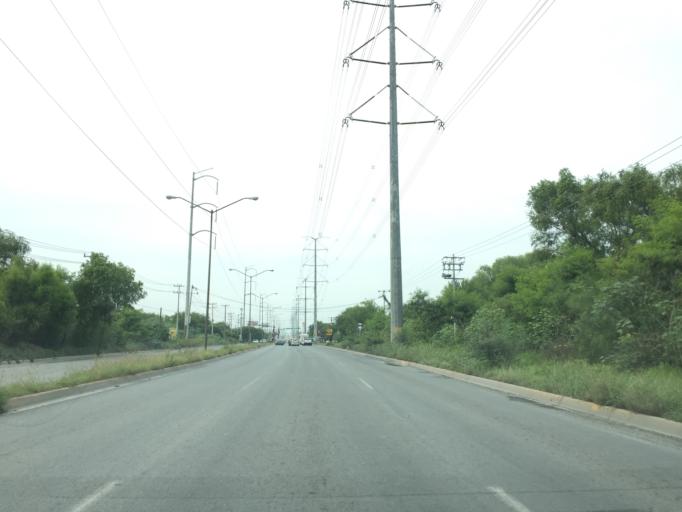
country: MX
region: Nuevo Leon
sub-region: Apodaca
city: Fraccionamiento Cosmopolis Octavo Sector
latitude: 25.7940
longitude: -100.2235
